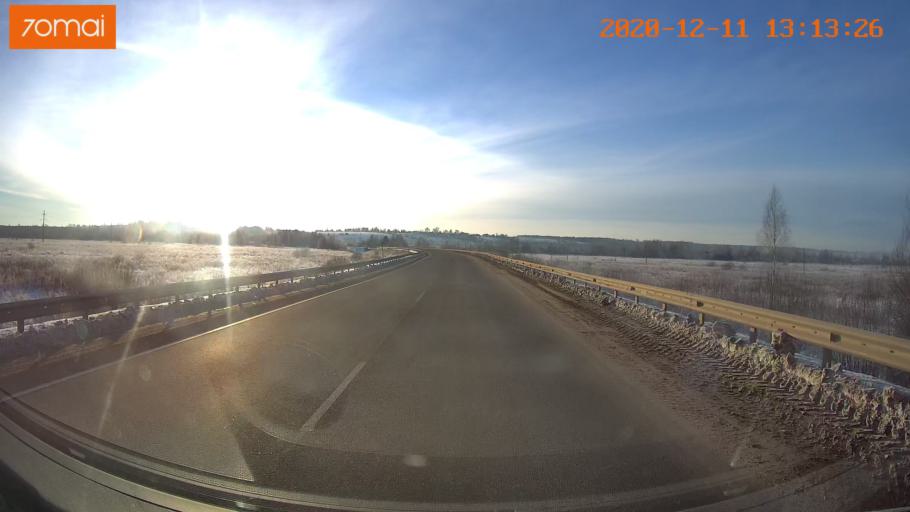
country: RU
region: Kostroma
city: Susanino
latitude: 58.1418
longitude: 41.6098
